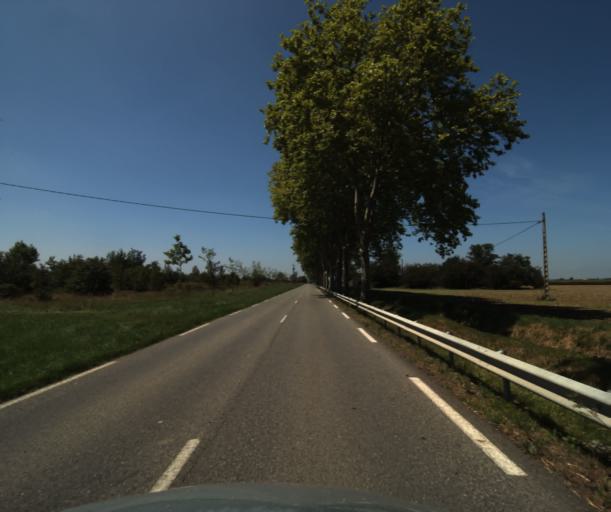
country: FR
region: Midi-Pyrenees
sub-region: Departement de la Haute-Garonne
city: Seysses
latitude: 43.4645
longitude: 1.2935
